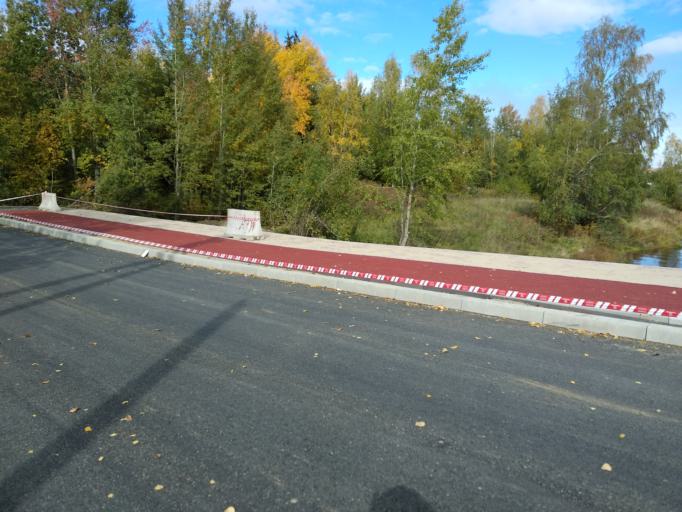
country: RU
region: Sverdlovsk
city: Krasnotur'insk
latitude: 59.7618
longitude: 60.1655
